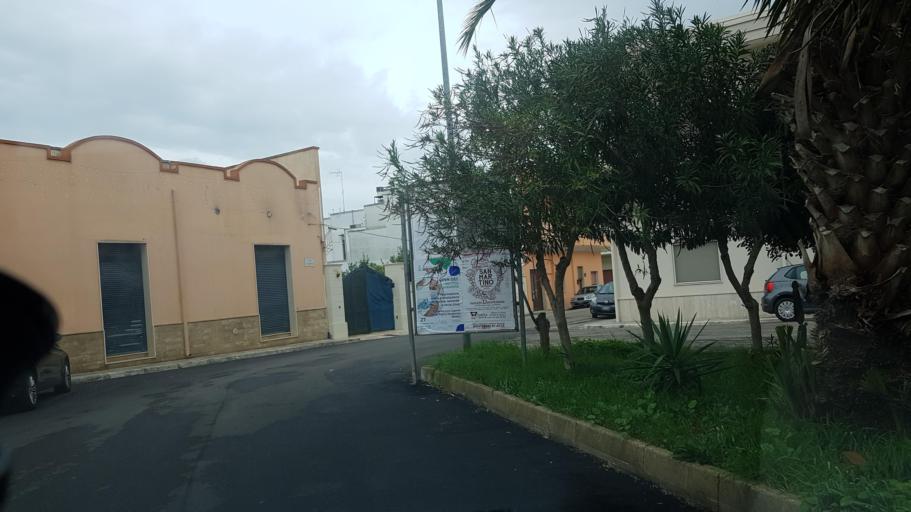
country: IT
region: Apulia
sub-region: Provincia di Lecce
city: Novoli
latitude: 40.3788
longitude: 18.0455
